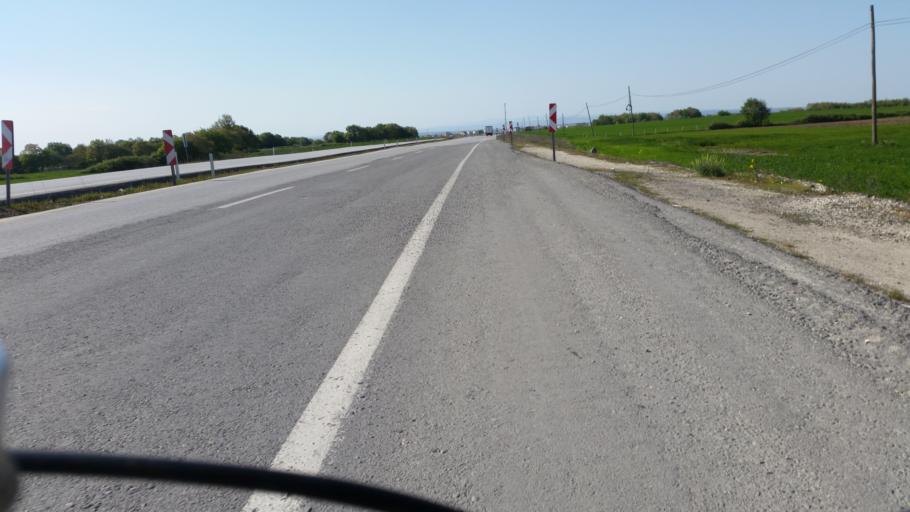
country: TR
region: Tekirdag
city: Cerkezkoey
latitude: 41.3439
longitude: 27.9627
